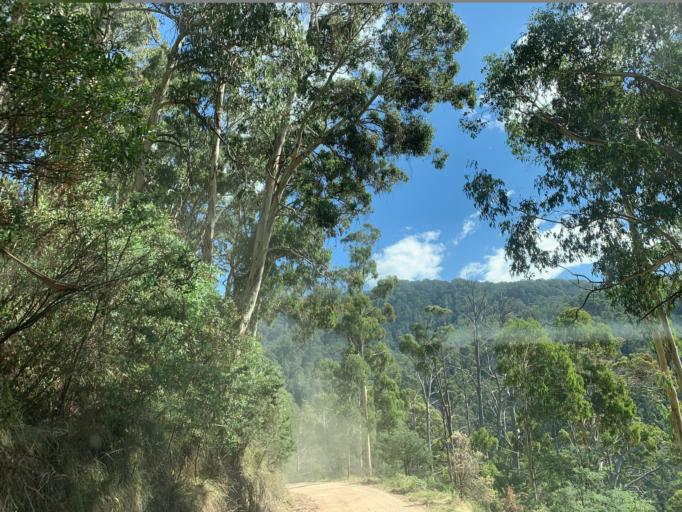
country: AU
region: Victoria
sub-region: Mansfield
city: Mansfield
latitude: -37.0994
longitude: 146.5053
